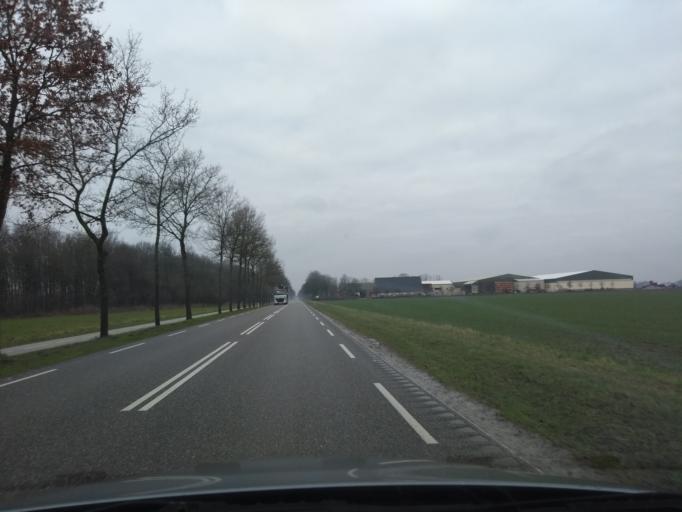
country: NL
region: Overijssel
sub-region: Gemeente Steenwijkerland
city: Vollenhove
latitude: 52.6896
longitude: 5.9327
